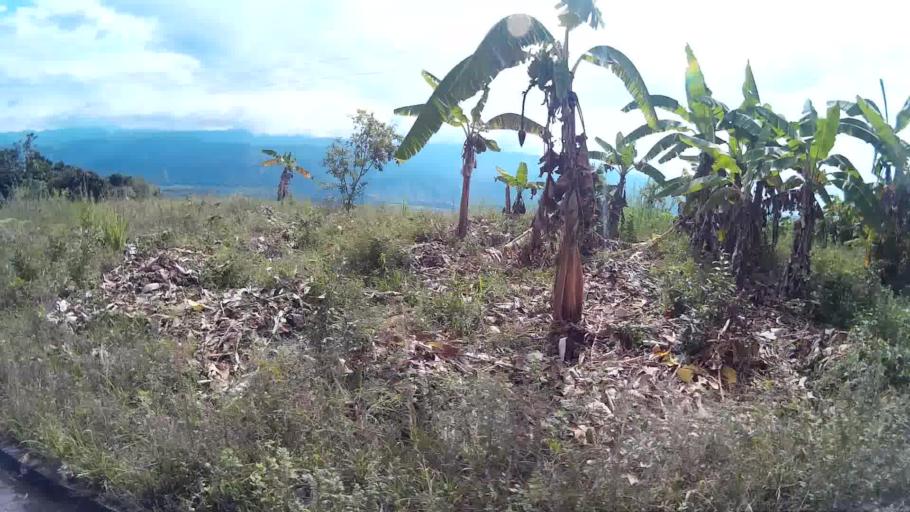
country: CO
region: Caldas
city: Belalcazar
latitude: 4.9506
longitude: -75.8343
